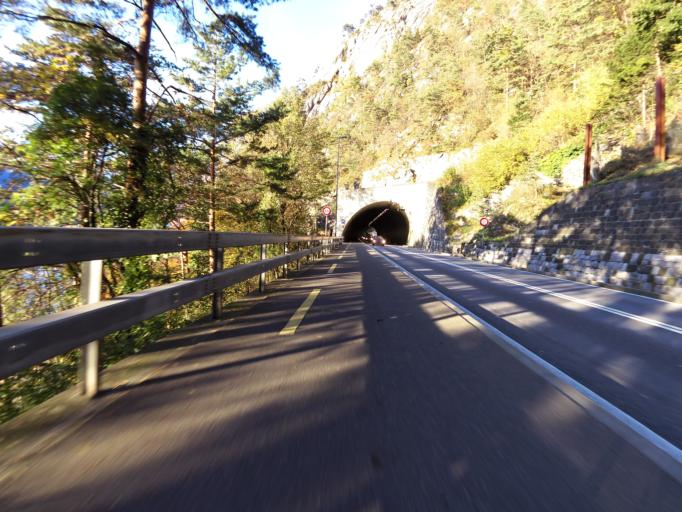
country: CH
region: Uri
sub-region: Uri
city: Bauen
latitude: 46.9450
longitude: 8.6205
